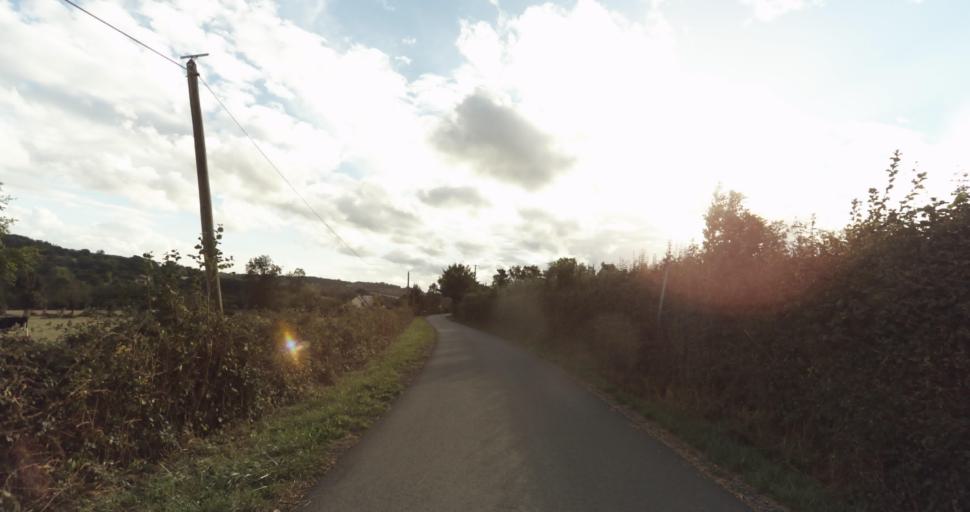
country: FR
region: Lower Normandy
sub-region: Departement de l'Orne
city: Sainte-Gauburge-Sainte-Colombe
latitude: 48.7199
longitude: 0.4187
